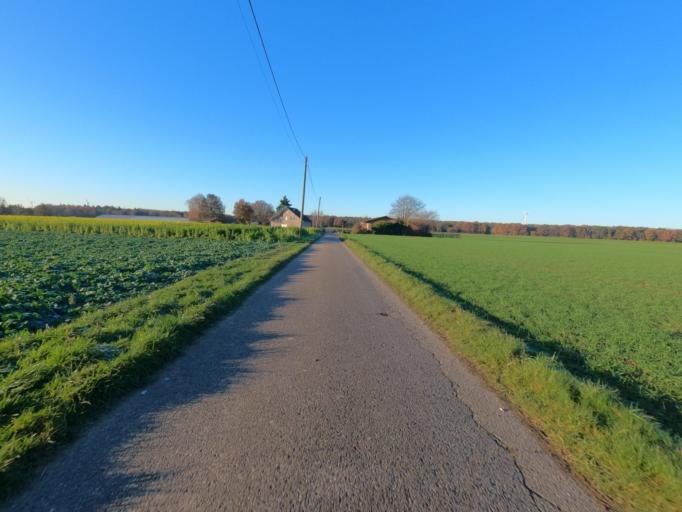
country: DE
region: North Rhine-Westphalia
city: Geilenkirchen
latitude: 50.9901
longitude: 6.0895
